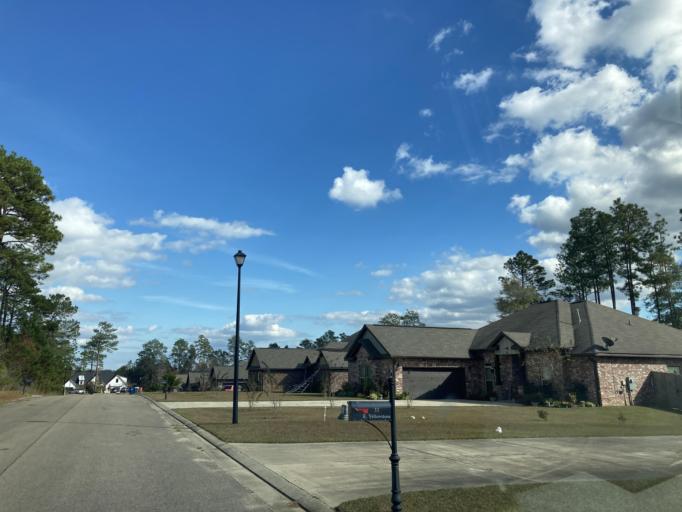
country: US
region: Mississippi
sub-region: Lamar County
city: Arnold Line
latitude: 31.3460
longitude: -89.3680
